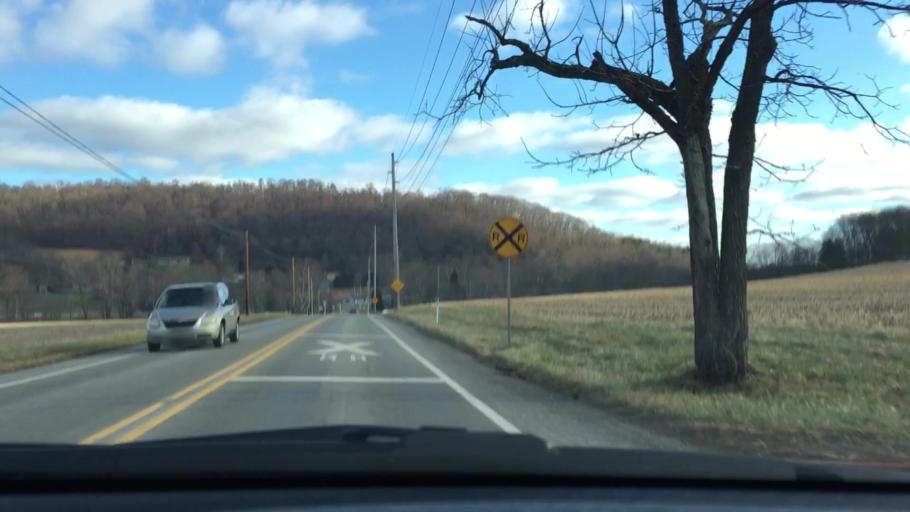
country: US
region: Pennsylvania
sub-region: Indiana County
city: Indiana
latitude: 40.6557
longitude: -79.3084
